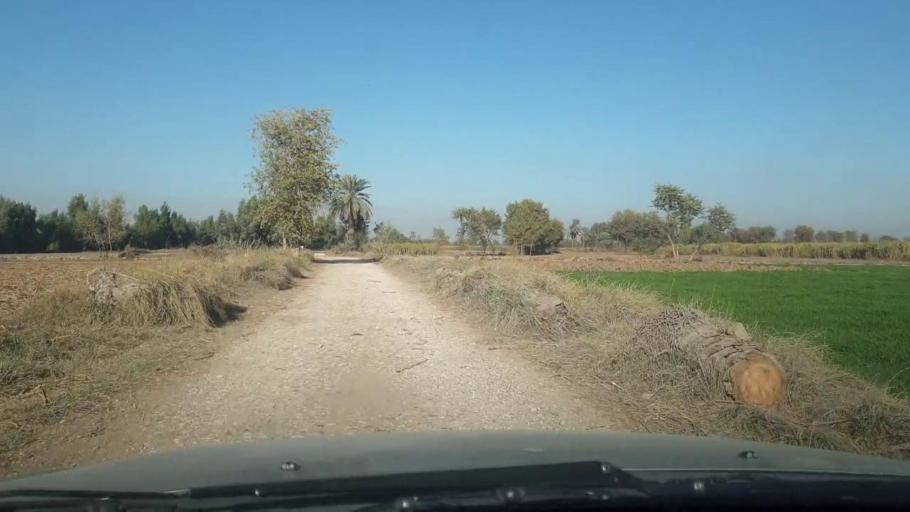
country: PK
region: Sindh
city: Adilpur
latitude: 27.9551
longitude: 69.1991
